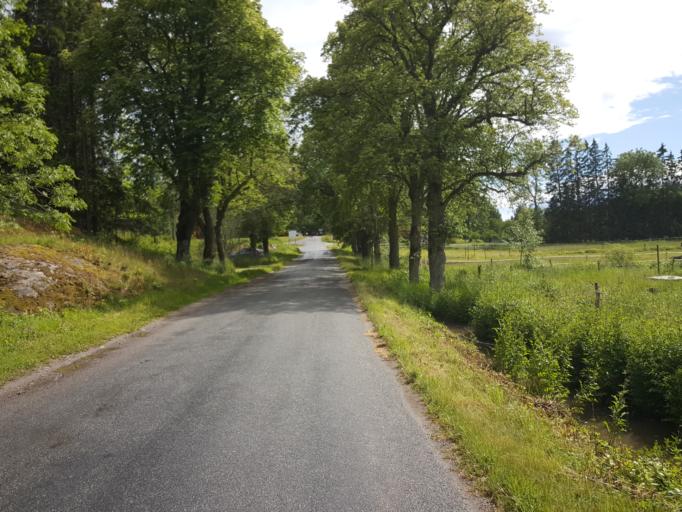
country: SE
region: Stockholm
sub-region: Nynashamns Kommun
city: Osmo
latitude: 59.0424
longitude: 18.0145
